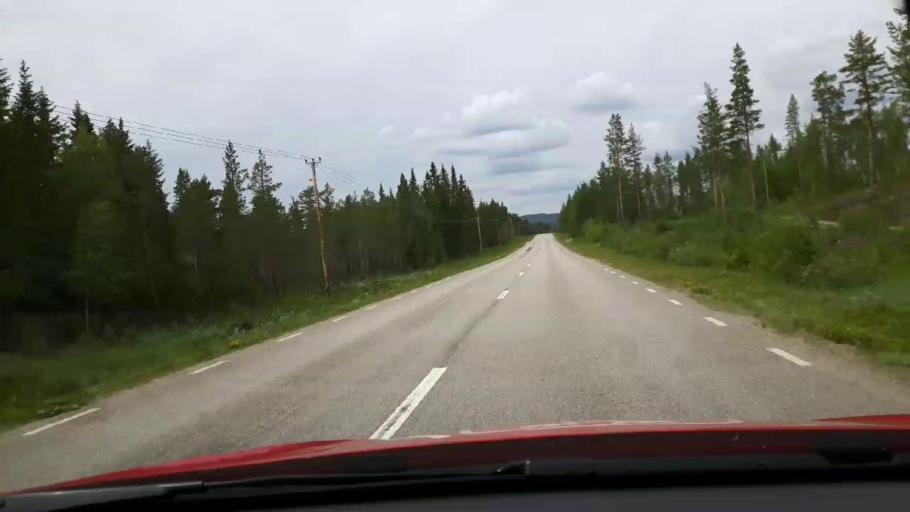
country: SE
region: Jaemtland
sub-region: Harjedalens Kommun
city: Sveg
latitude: 62.3943
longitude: 13.7536
